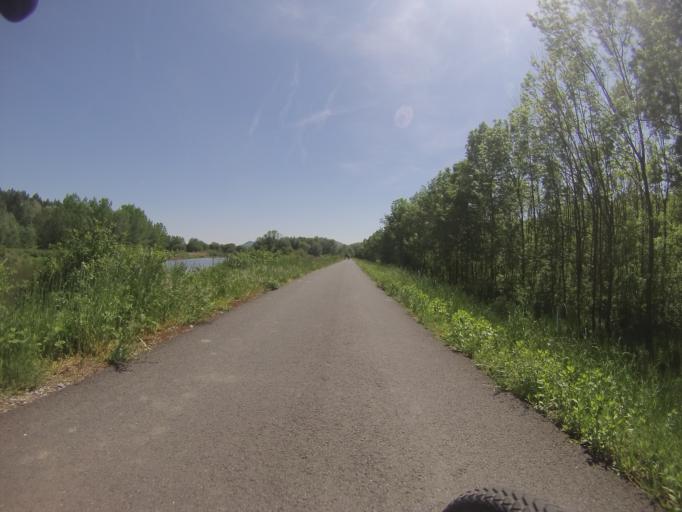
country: CZ
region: South Moravian
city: Vranovice
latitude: 48.9148
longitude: 16.6012
